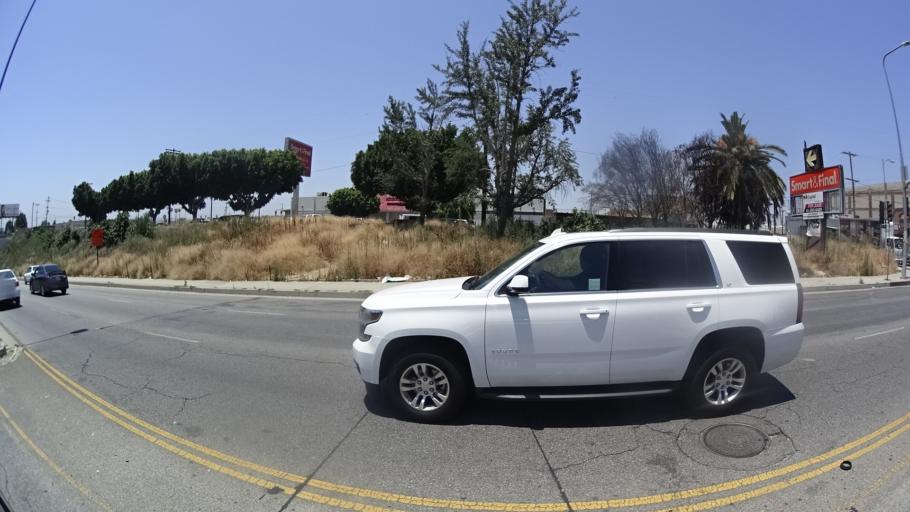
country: US
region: California
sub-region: Los Angeles County
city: Van Nuys
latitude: 34.2131
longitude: -118.4488
